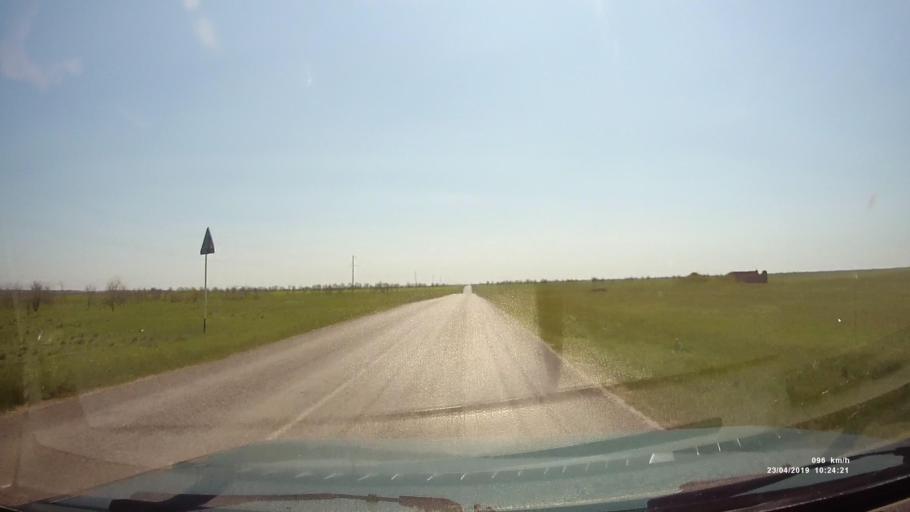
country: RU
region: Rostov
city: Sovetskoye
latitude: 46.6395
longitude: 42.4403
